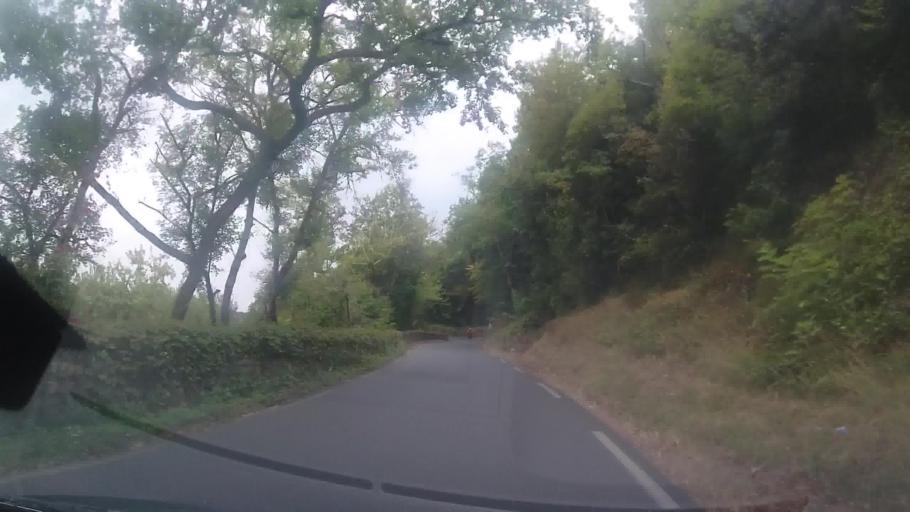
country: FR
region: Aquitaine
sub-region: Departement de la Dordogne
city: Carsac-Aillac
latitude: 44.8431
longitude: 1.2666
